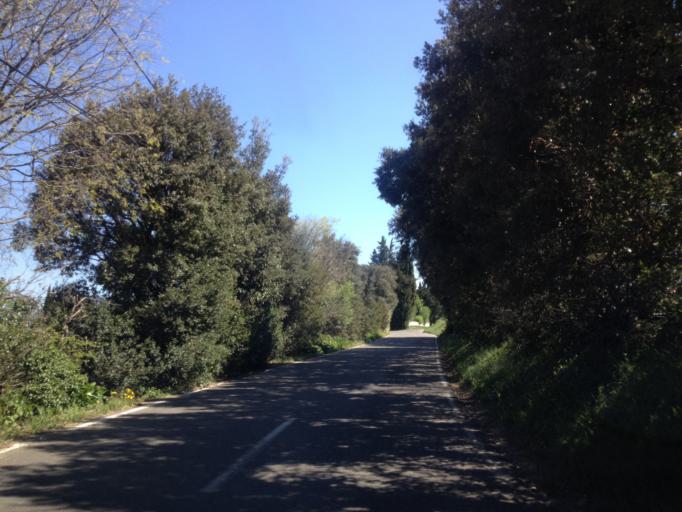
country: FR
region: Provence-Alpes-Cote d'Azur
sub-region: Departement du Vaucluse
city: Orange
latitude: 44.1081
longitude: 4.8164
